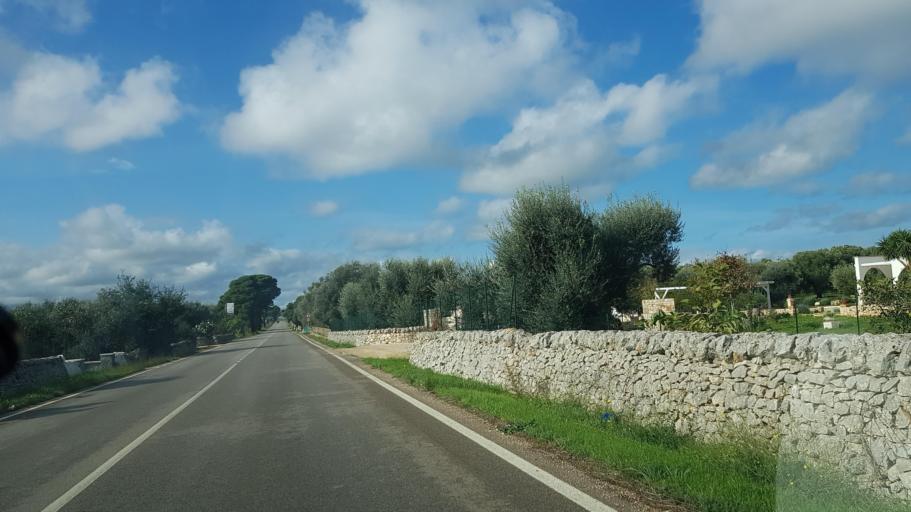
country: IT
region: Apulia
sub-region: Provincia di Brindisi
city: Carovigno
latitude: 40.7120
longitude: 17.6327
